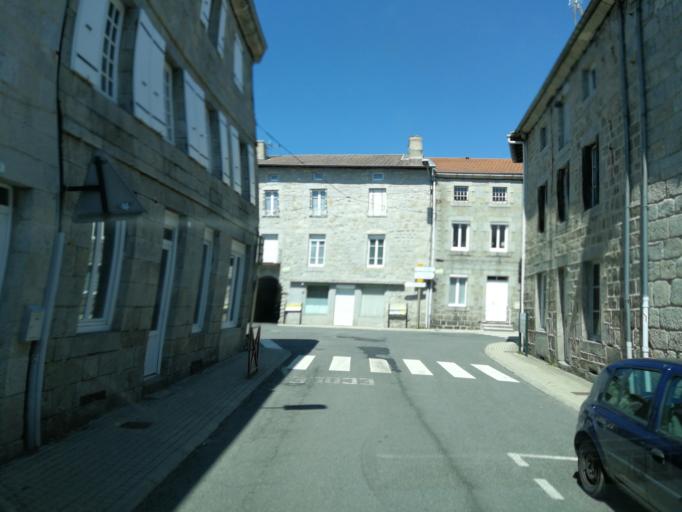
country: FR
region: Rhone-Alpes
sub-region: Departement de la Loire
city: Marlhes
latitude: 45.2836
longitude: 4.3944
